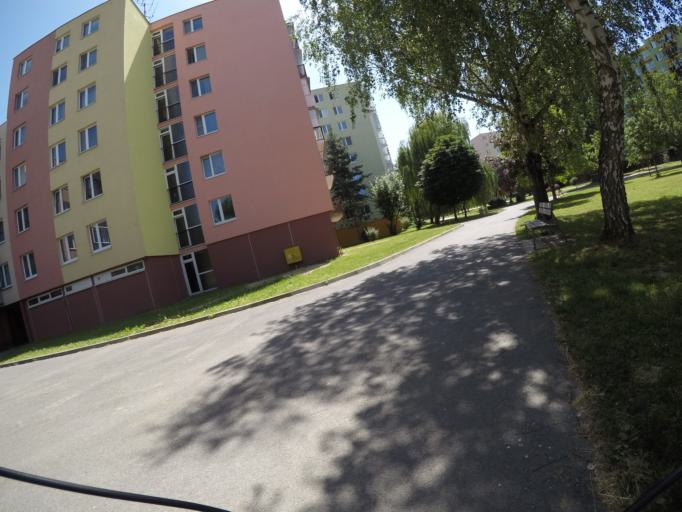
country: SK
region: Trenciansky
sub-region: Okres Nove Mesto nad Vahom
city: Nove Mesto nad Vahom
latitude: 48.7542
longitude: 17.8224
